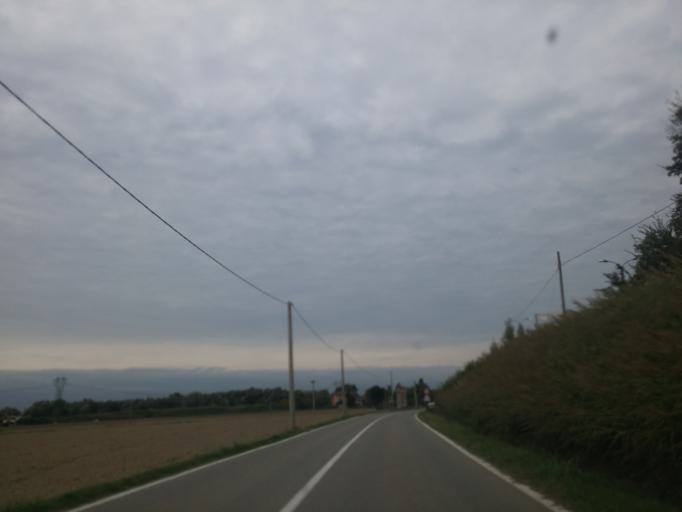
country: IT
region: Emilia-Romagna
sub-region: Provincia di Bologna
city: Longara
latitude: 44.5931
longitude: 11.3220
